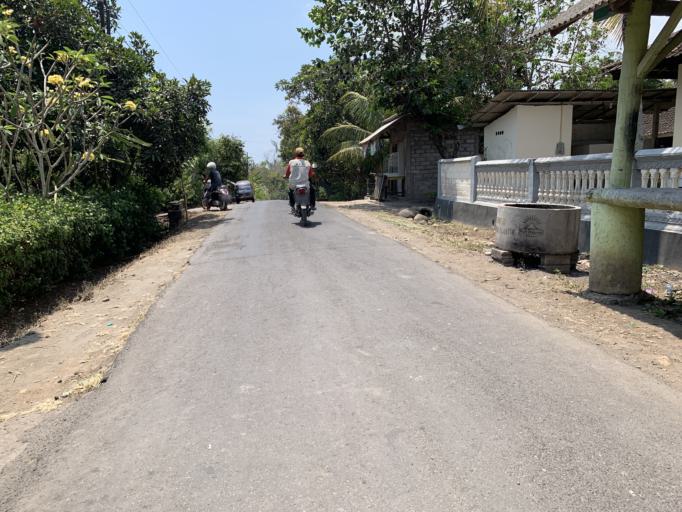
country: ID
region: Bali
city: Pekutatan
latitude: -8.4283
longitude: 114.8224
